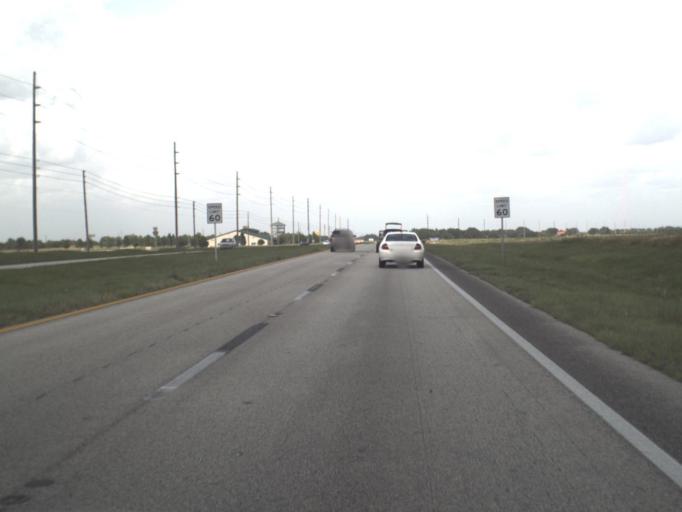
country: US
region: Florida
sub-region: Polk County
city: Lake Wales
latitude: 27.8738
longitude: -81.5947
